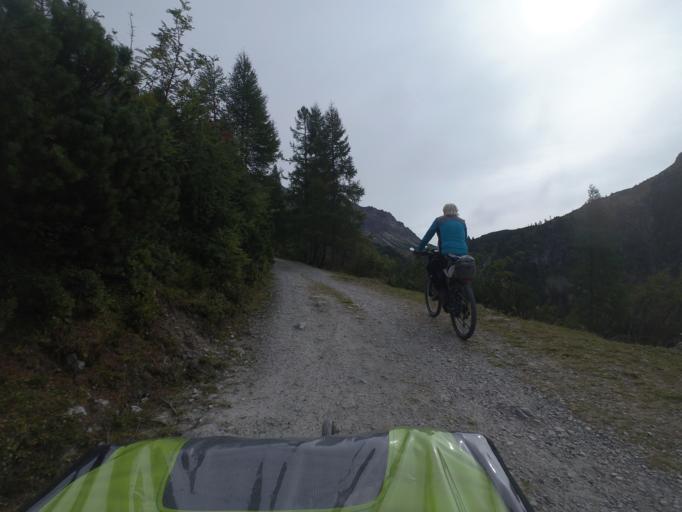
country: AT
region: Salzburg
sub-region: Politischer Bezirk Sankt Johann im Pongau
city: Untertauern
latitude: 47.2912
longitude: 13.5905
